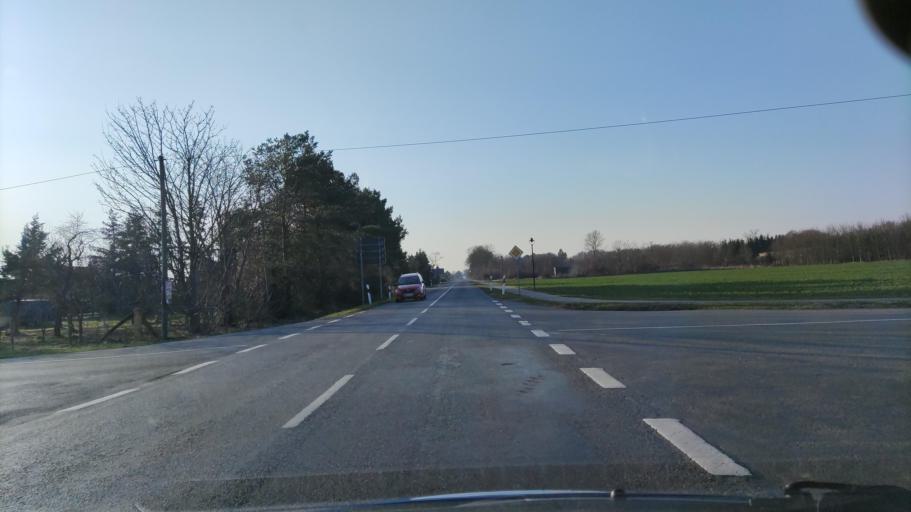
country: DE
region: Brandenburg
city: Cumlosen
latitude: 52.9516
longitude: 11.6531
